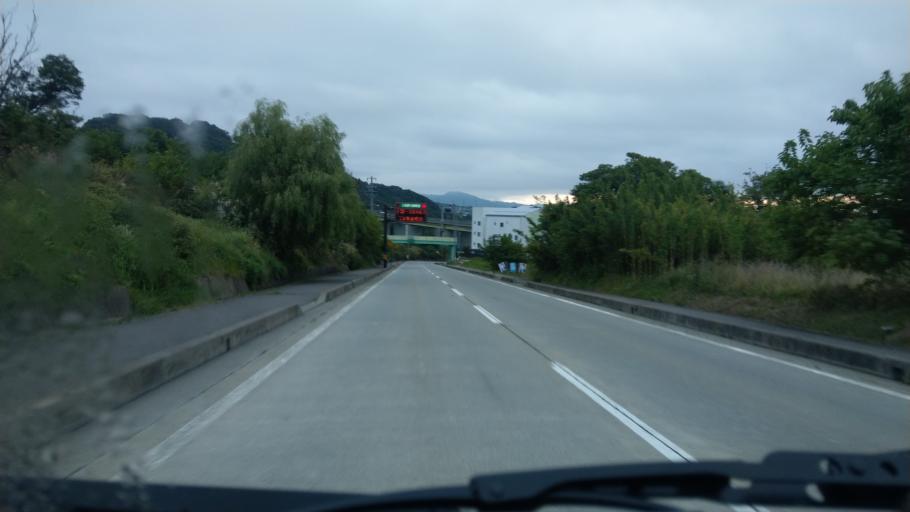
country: JP
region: Nagano
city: Komoro
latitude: 36.3474
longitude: 138.4084
